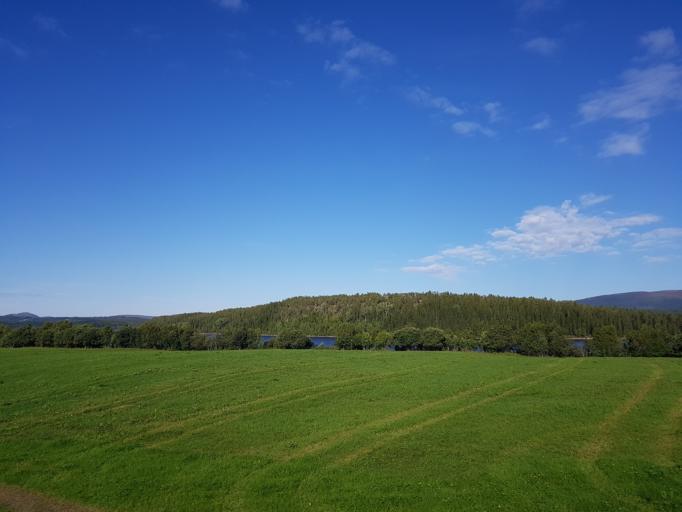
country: NO
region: Sor-Trondelag
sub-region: Trondheim
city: Trondheim
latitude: 63.6206
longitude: 10.2391
